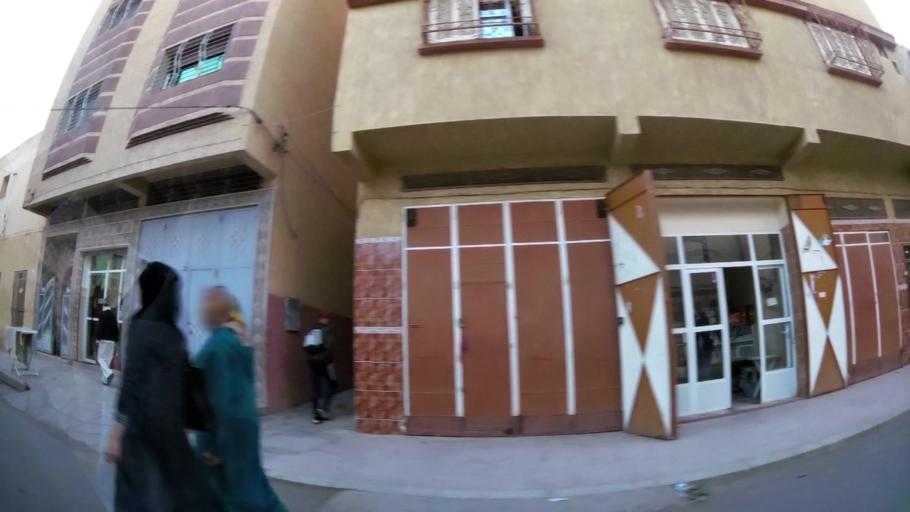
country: MA
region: Oriental
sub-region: Oujda-Angad
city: Oujda
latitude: 34.6996
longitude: -1.9206
